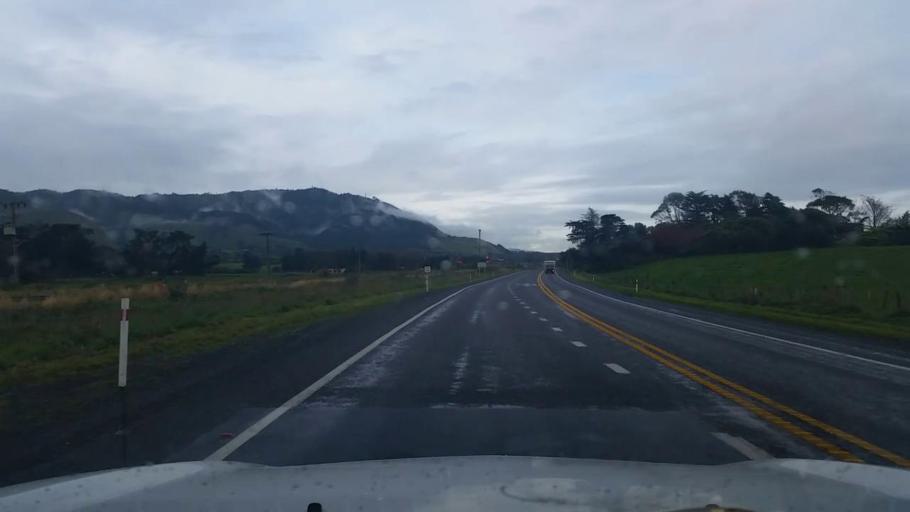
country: NZ
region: Wellington
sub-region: Kapiti Coast District
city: Otaki
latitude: -40.8059
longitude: 175.1183
